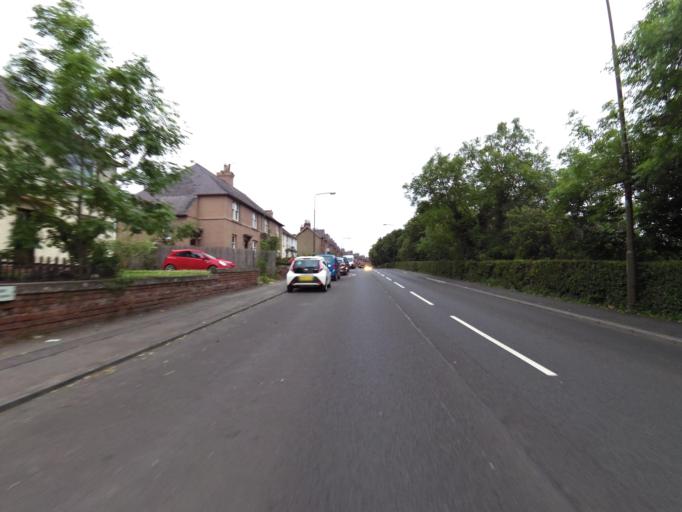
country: GB
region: Scotland
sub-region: East Lothian
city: Musselburgh
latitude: 55.9339
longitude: -3.0608
